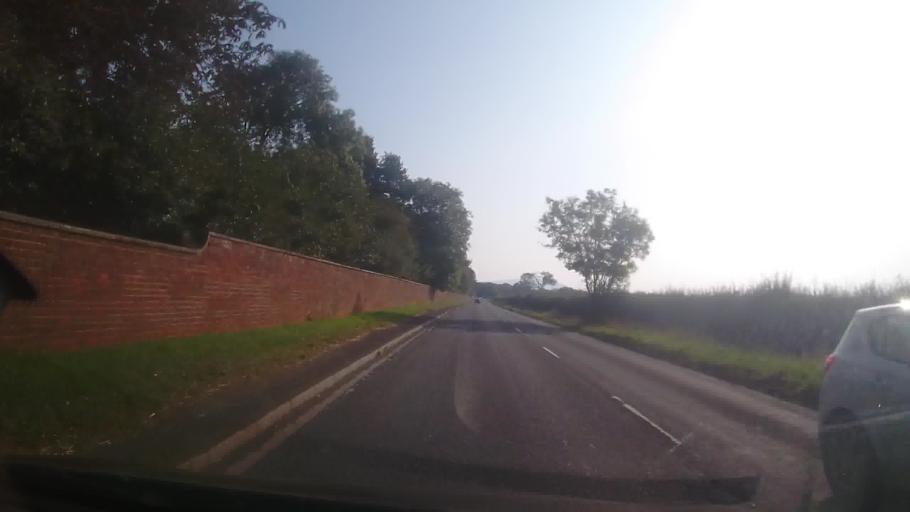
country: GB
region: England
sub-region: Shropshire
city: Berrington
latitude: 52.6799
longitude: -2.6728
